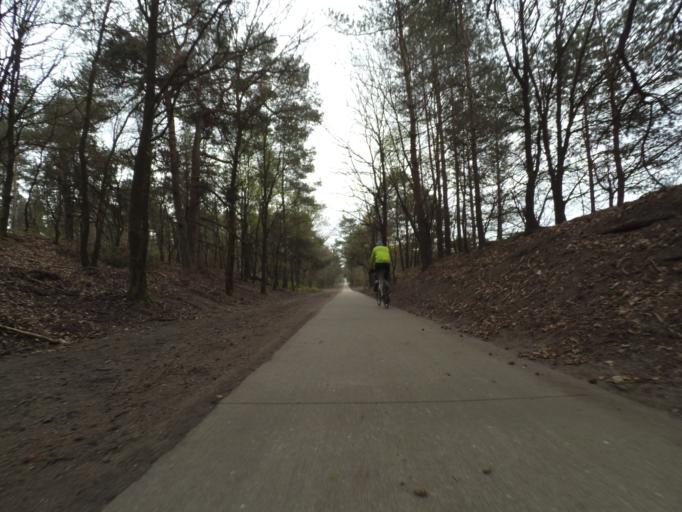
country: NL
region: Gelderland
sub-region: Gemeente Nunspeet
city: Nunspeet
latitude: 52.3439
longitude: 5.8782
